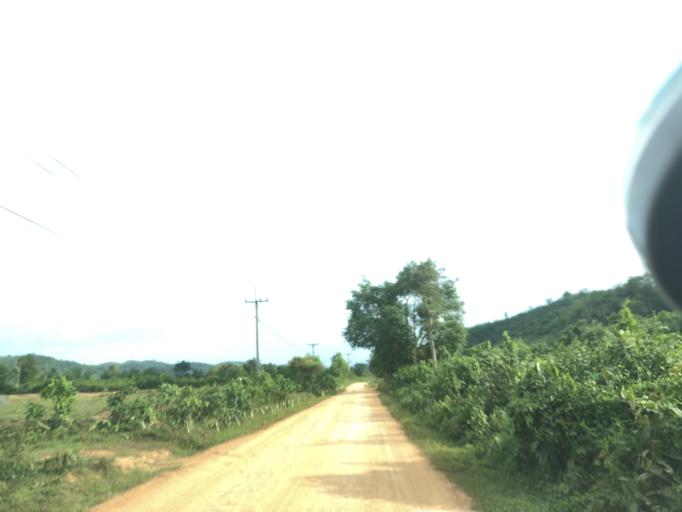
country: TH
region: Loei
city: Chiang Khan
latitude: 18.0013
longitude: 101.4200
